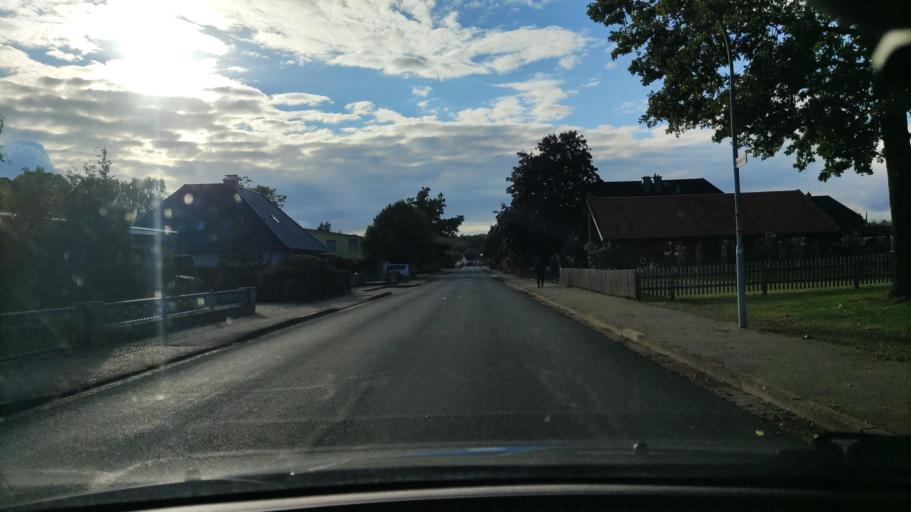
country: DE
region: Lower Saxony
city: Munster
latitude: 53.0046
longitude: 10.0986
